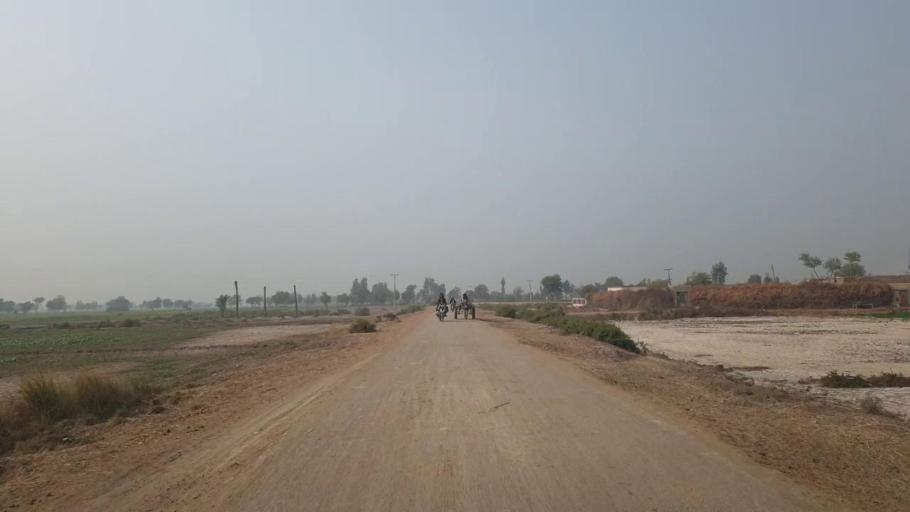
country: PK
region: Sindh
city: Shahdadpur
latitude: 25.8400
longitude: 68.5791
